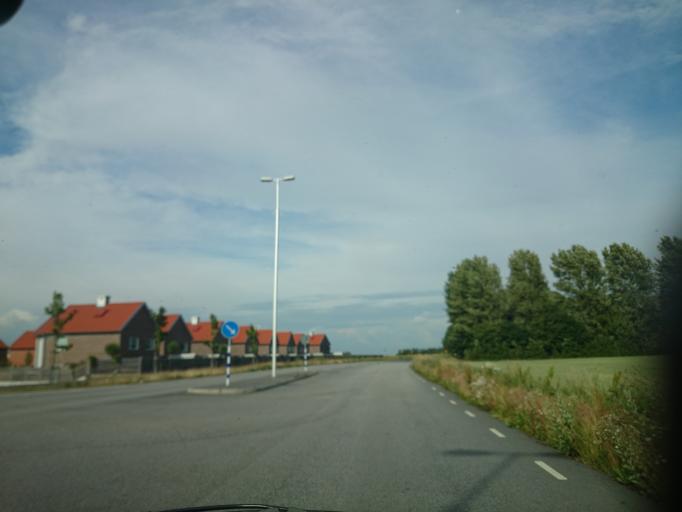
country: SE
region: Skane
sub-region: Lunds Kommun
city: Lund
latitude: 55.7496
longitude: 13.2049
